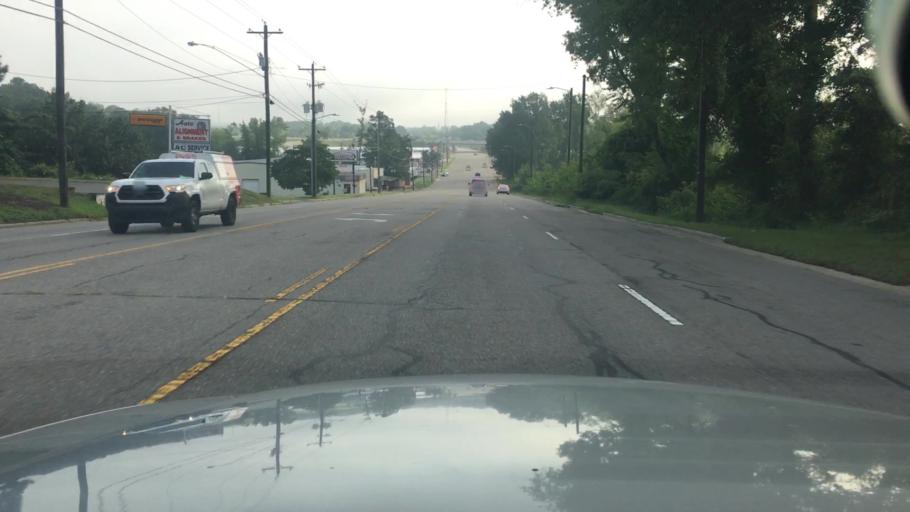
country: US
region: North Carolina
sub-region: Cumberland County
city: Fayetteville
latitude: 35.0315
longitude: -78.8868
